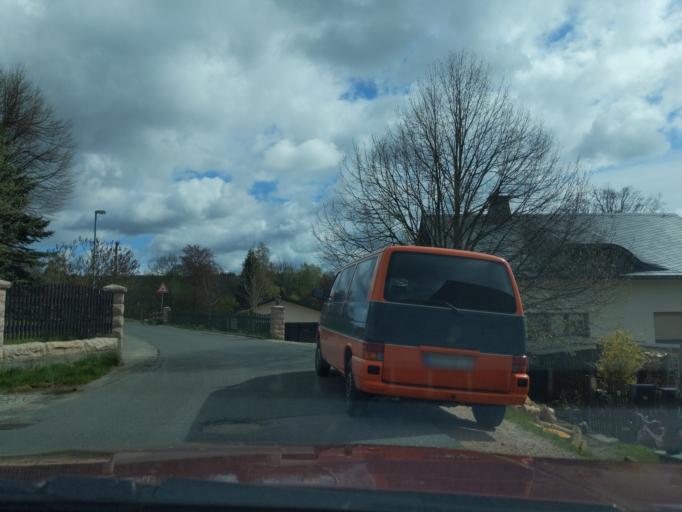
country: DE
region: Saxony
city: Schoenheide
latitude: 50.5045
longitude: 12.5370
